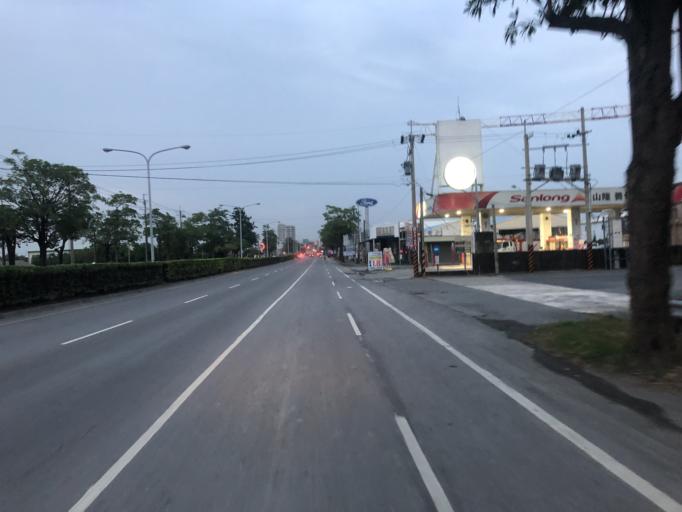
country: TW
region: Taiwan
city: Yujing
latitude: 23.1158
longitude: 120.3185
